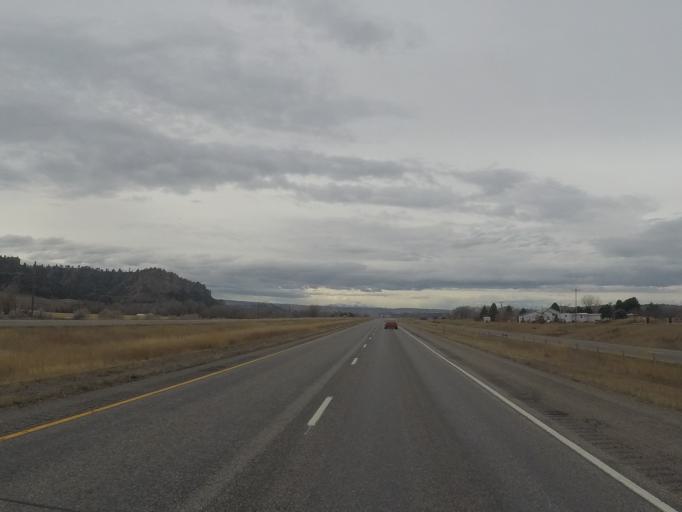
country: US
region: Montana
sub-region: Yellowstone County
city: Laurel
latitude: 45.6176
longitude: -108.9927
